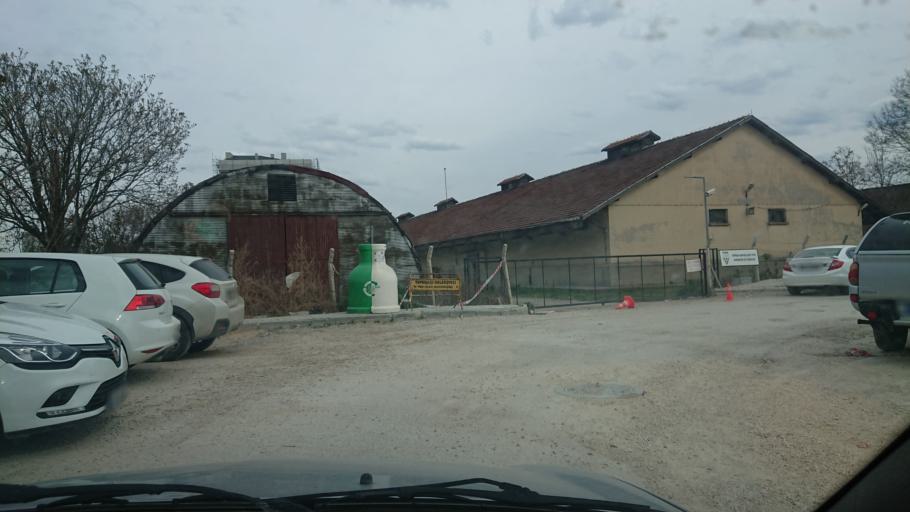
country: TR
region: Eskisehir
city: Eskisehir
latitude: 39.7818
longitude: 30.5067
